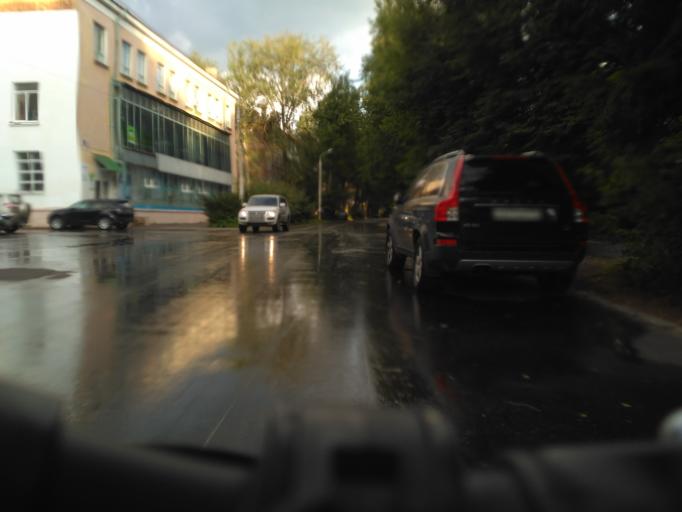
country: RU
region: Moskovskaya
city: Dubna
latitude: 56.7500
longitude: 37.1910
